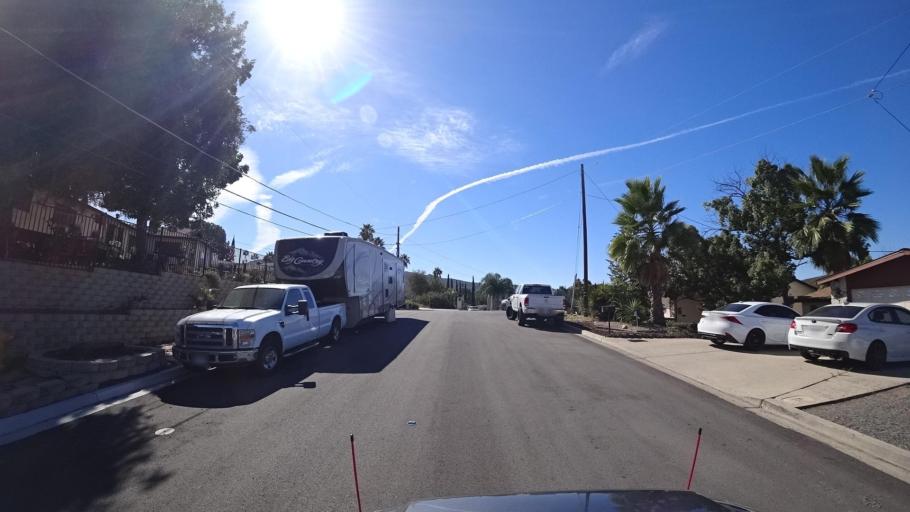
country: US
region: California
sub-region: San Diego County
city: Lakeside
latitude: 32.8416
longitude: -116.8996
